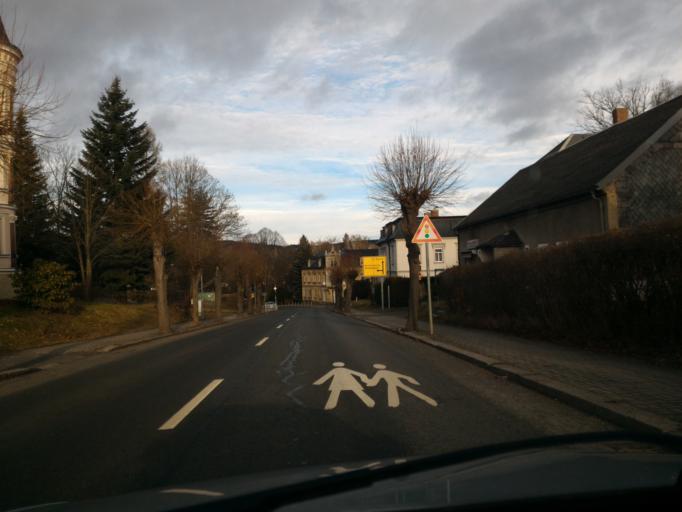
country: DE
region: Saxony
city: Oppach
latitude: 51.0574
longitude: 14.5040
